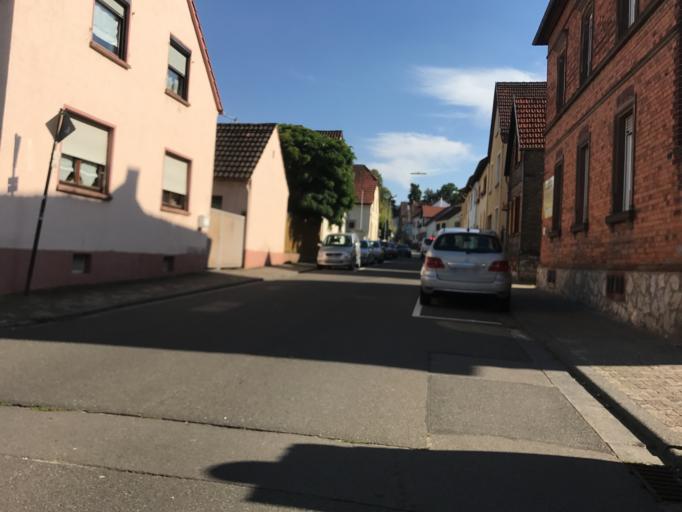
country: DE
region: Rheinland-Pfalz
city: Wackernheim
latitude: 49.9957
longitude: 8.1089
